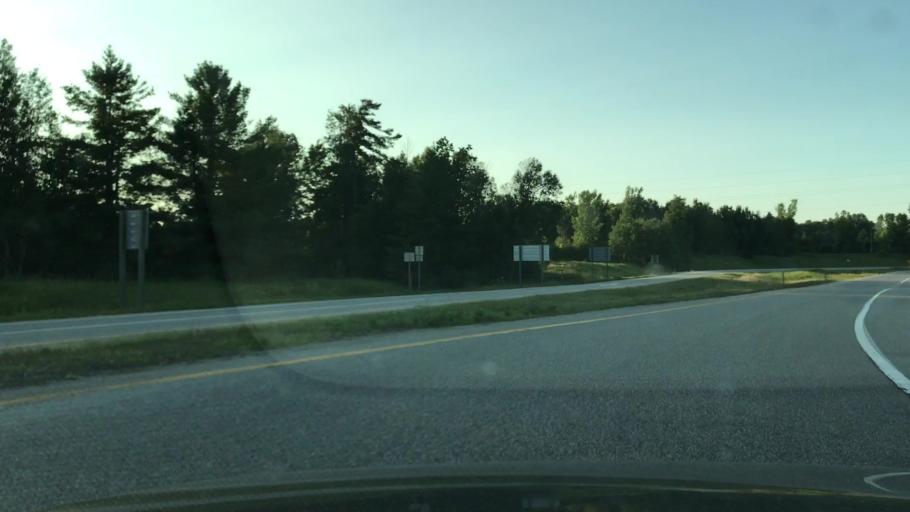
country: US
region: Michigan
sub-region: Osceola County
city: Reed City
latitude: 43.8878
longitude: -85.5317
